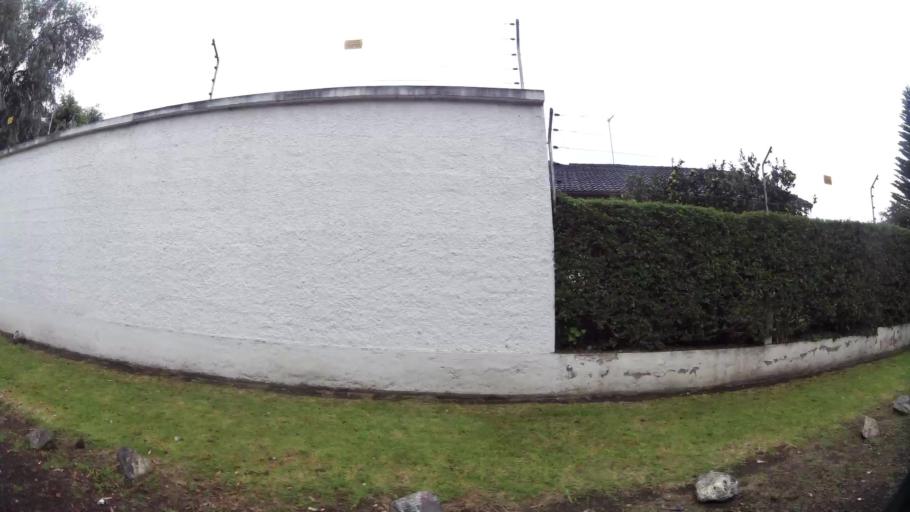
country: EC
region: Pichincha
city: Sangolqui
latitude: -0.2854
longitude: -78.4548
